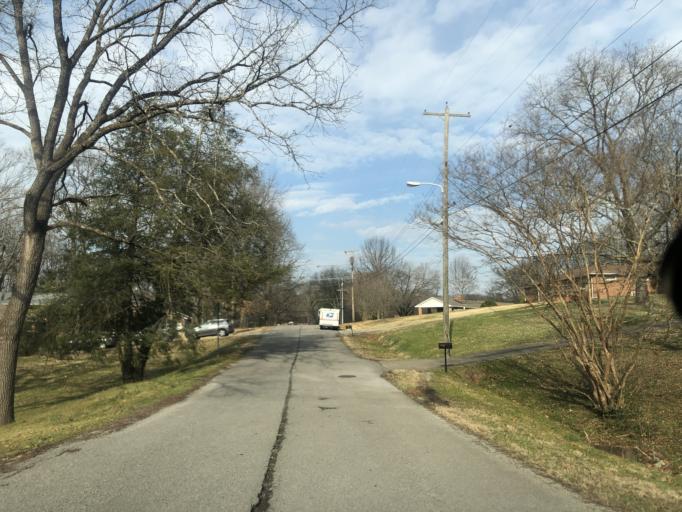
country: US
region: Tennessee
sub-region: Davidson County
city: Oak Hill
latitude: 36.1036
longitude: -86.7022
